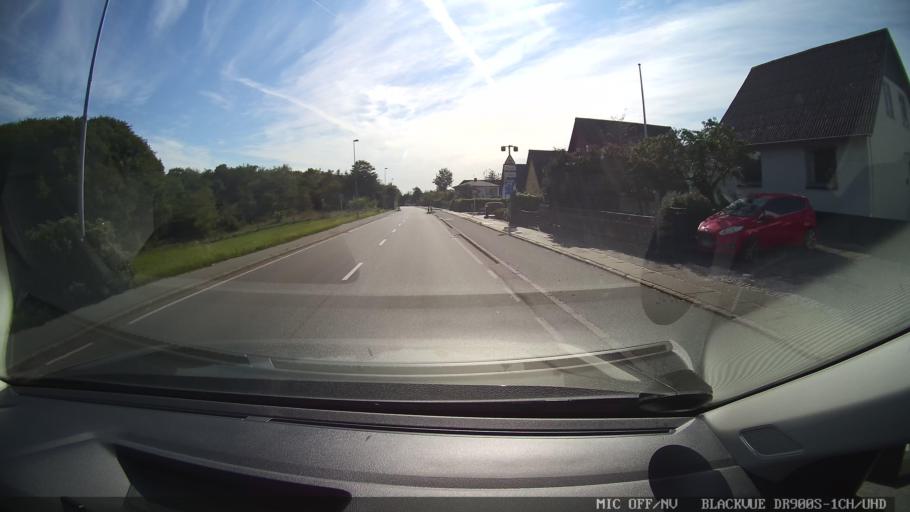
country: DK
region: North Denmark
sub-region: Mariagerfjord Kommune
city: Arden
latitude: 56.7656
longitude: 9.8673
